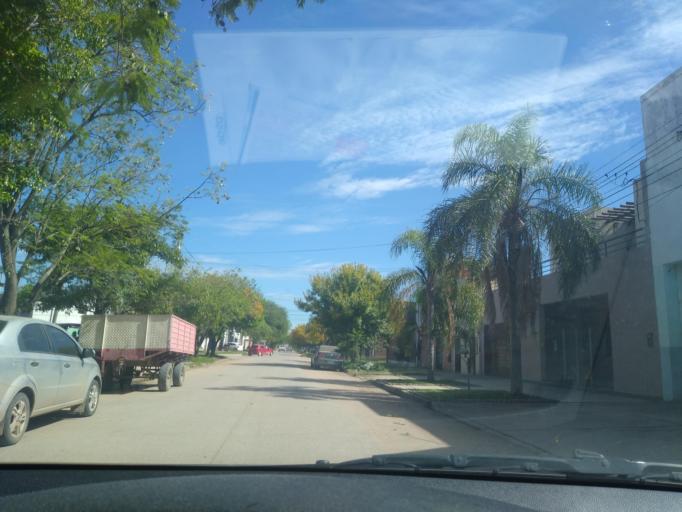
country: AR
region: Chaco
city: Presidencia Roque Saenz Pena
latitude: -26.7812
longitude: -60.4344
